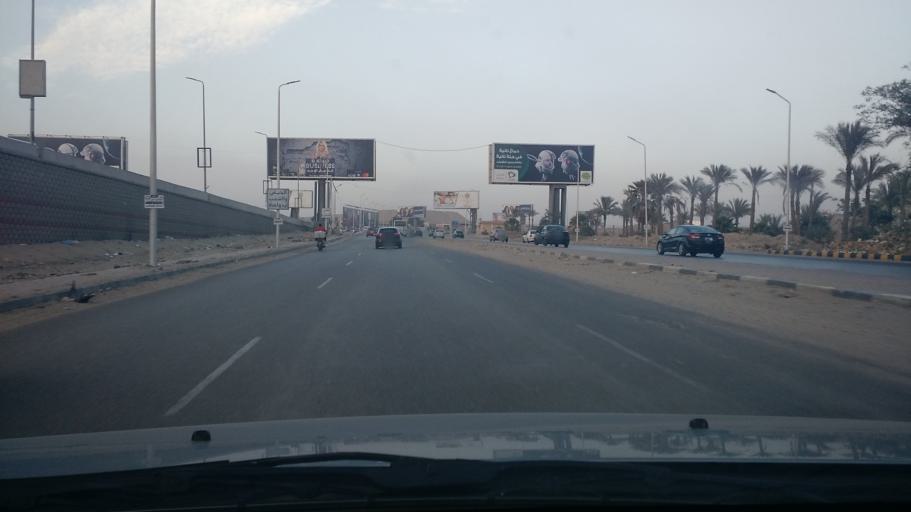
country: EG
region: Muhafazat al Qahirah
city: Cairo
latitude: 30.0239
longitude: 31.3570
